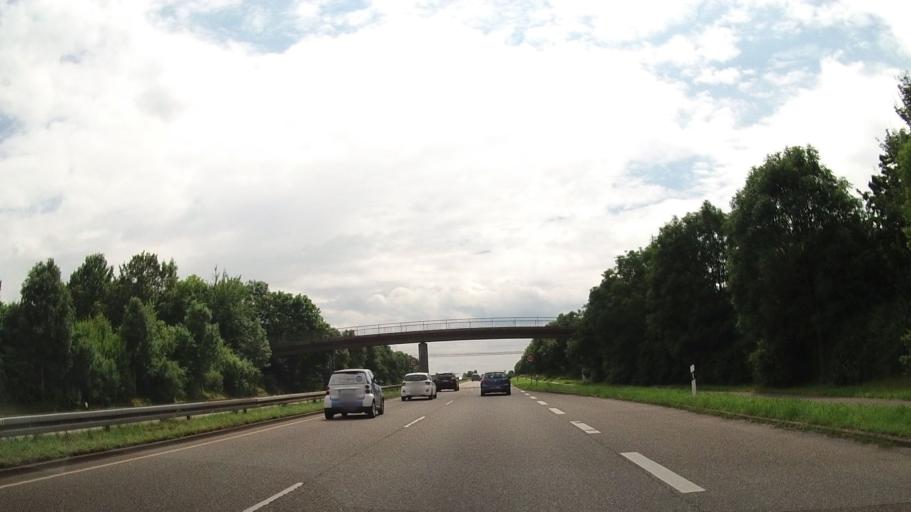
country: DE
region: Baden-Wuerttemberg
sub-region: Karlsruhe Region
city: Rheinstetten
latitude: 48.9924
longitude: 8.3404
